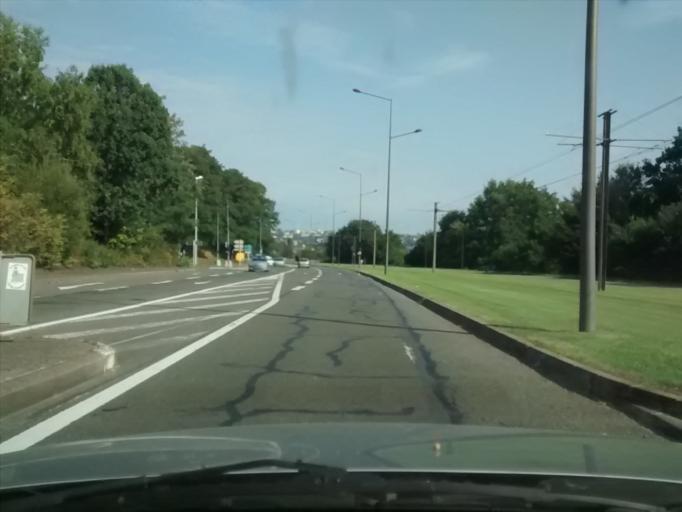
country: FR
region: Pays de la Loire
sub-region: Departement de la Sarthe
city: La Chapelle-Saint-Aubin
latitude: 48.0195
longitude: 0.1662
